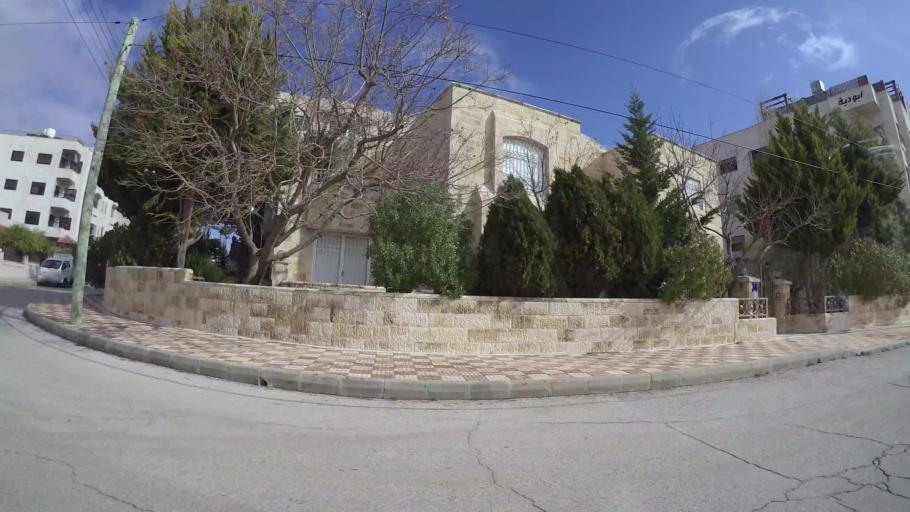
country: JO
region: Amman
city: Wadi as Sir
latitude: 31.9500
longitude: 35.8455
